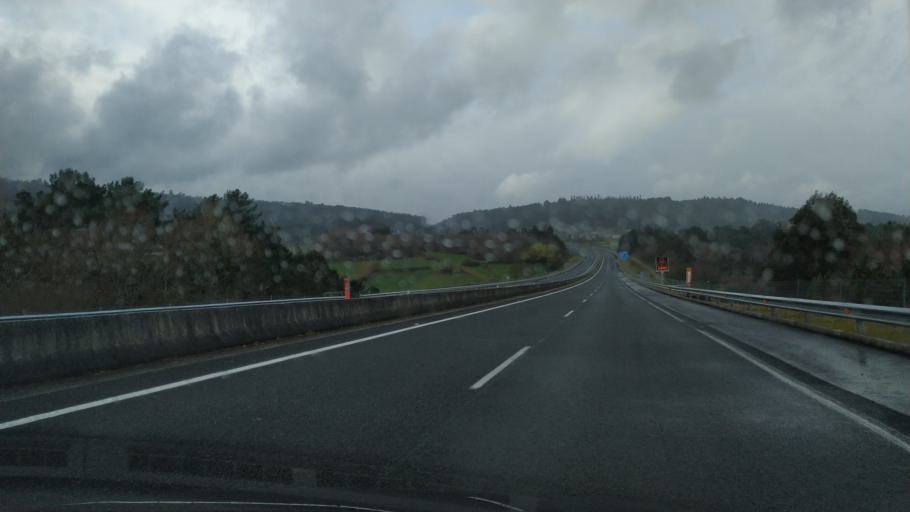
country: ES
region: Galicia
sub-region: Provincia de Pontevedra
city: Silleda
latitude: 42.7251
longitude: -8.3196
